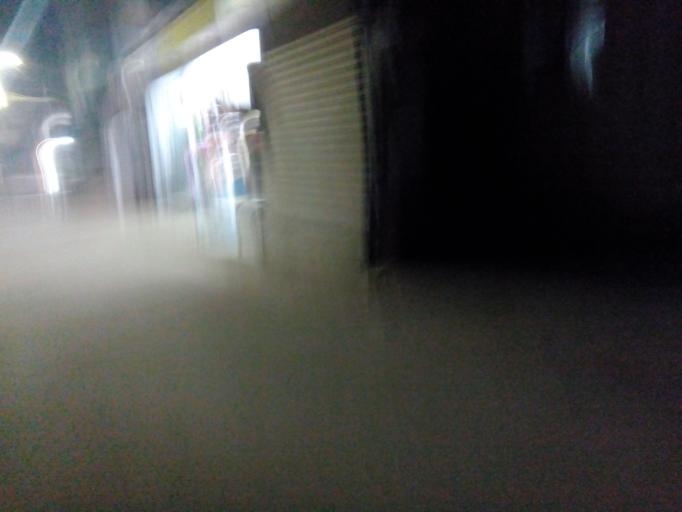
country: BD
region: Dhaka
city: Paltan
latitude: 23.7437
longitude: 90.4219
